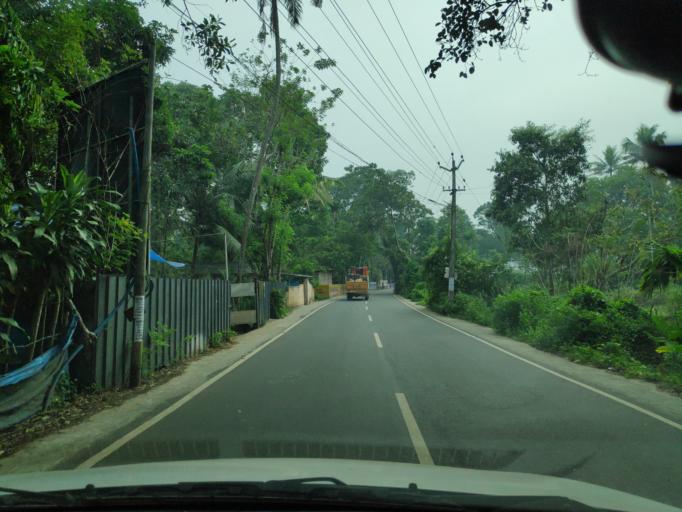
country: IN
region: Kerala
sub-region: Alappuzha
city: Shertallai
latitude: 9.6080
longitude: 76.3438
